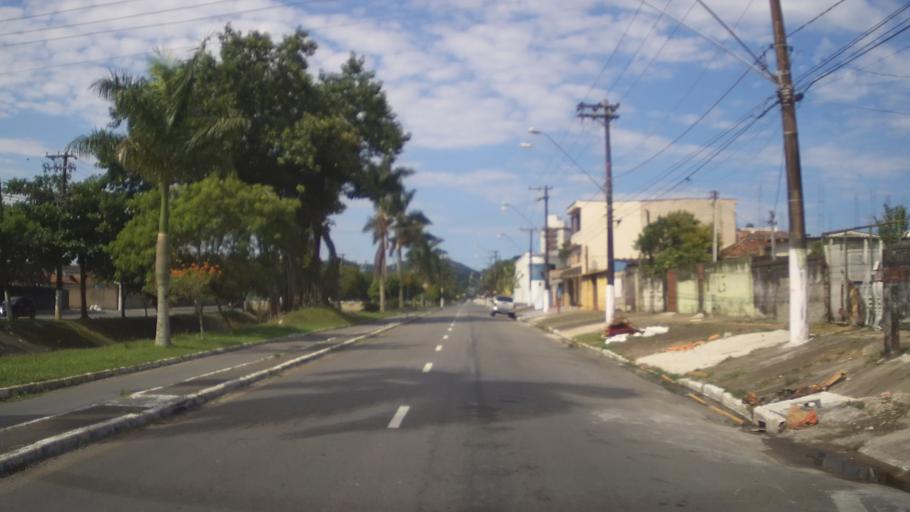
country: BR
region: Sao Paulo
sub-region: Praia Grande
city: Praia Grande
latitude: -24.0013
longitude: -46.4248
